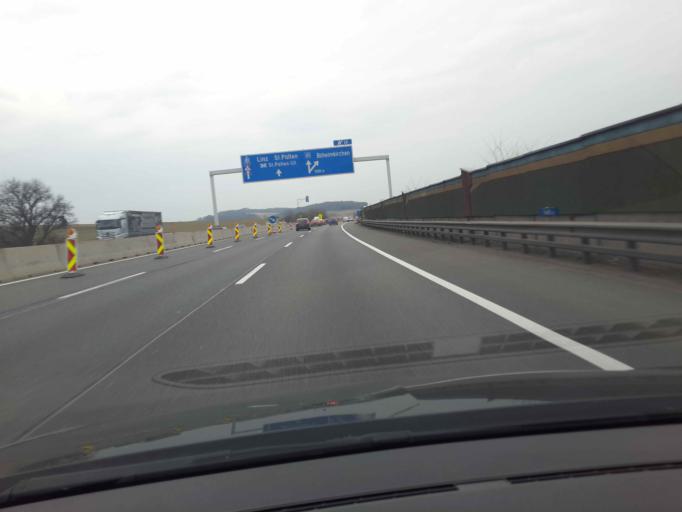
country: AT
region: Lower Austria
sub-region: Politischer Bezirk Sankt Polten
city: Boheimkirchen
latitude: 48.1842
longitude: 15.7752
